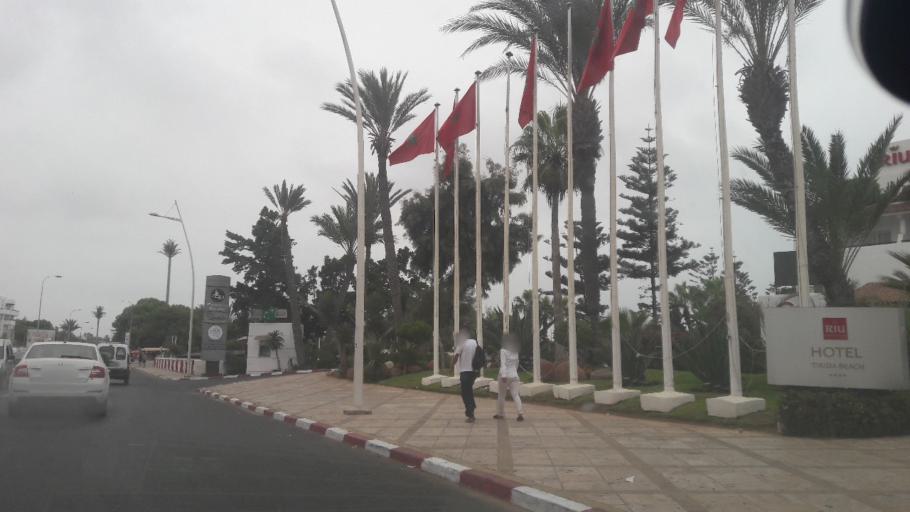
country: MA
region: Souss-Massa-Draa
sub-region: Agadir-Ida-ou-Tnan
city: Agadir
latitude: 30.4029
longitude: -9.5982
